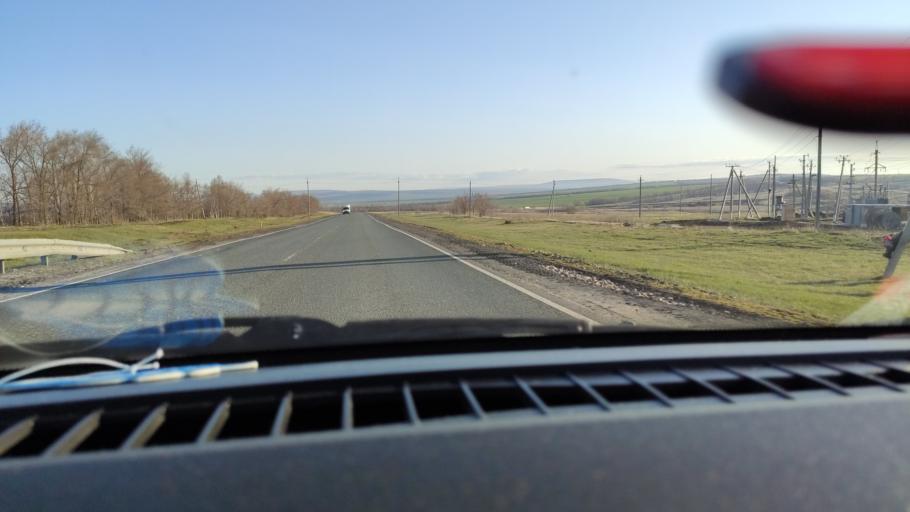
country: RU
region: Saratov
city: Balakovo
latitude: 52.1192
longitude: 47.7522
